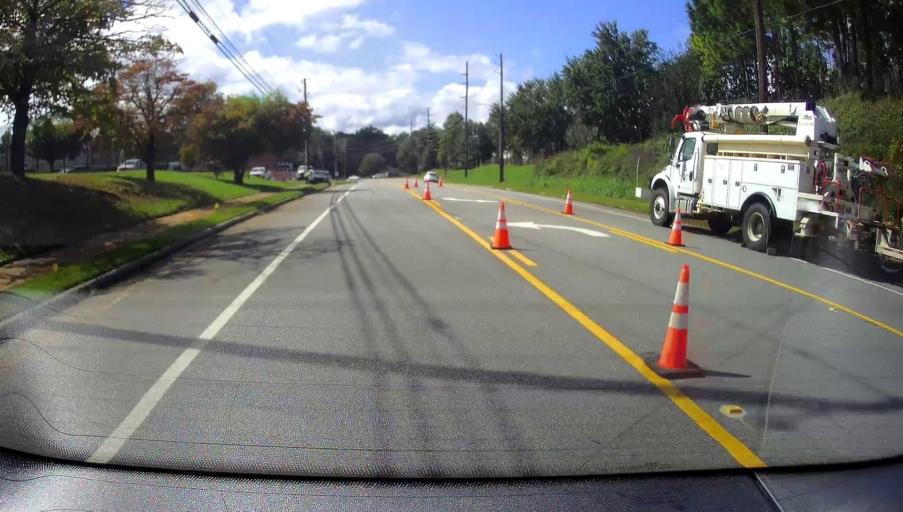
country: US
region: Georgia
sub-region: Baldwin County
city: Milledgeville
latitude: 33.0787
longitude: -83.2399
